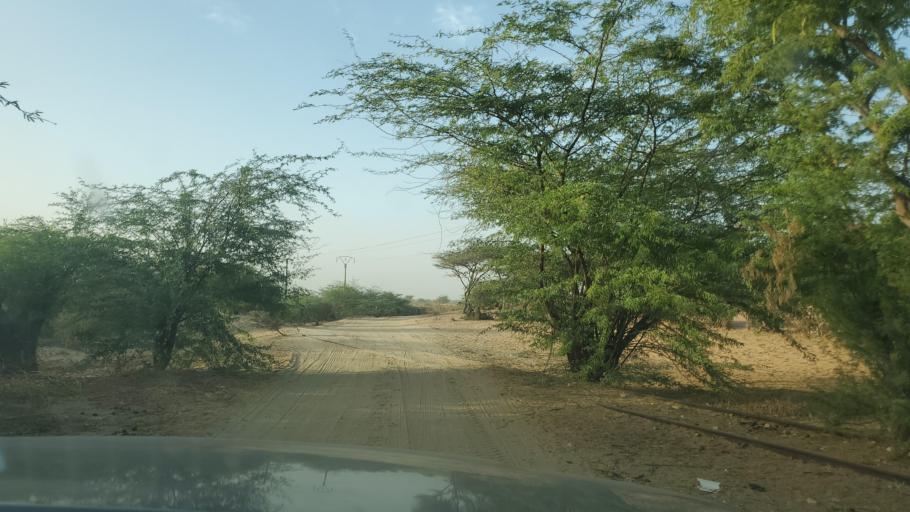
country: SN
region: Saint-Louis
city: Saint-Louis
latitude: 15.9194
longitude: -16.4189
